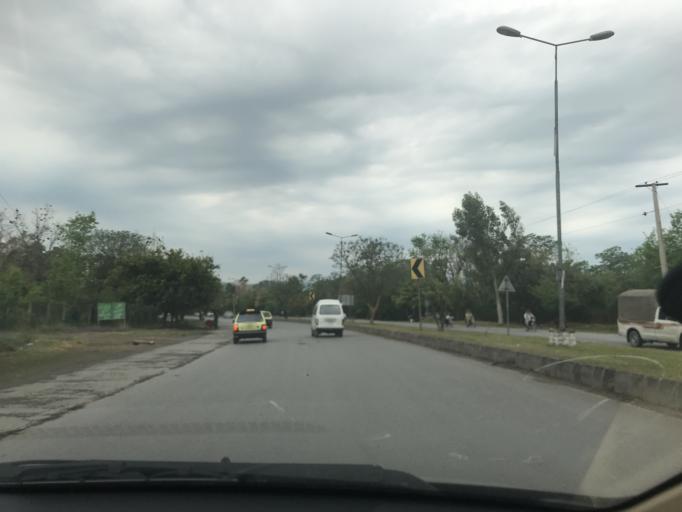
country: PK
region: Islamabad
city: Islamabad
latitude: 33.6858
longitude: 73.1344
